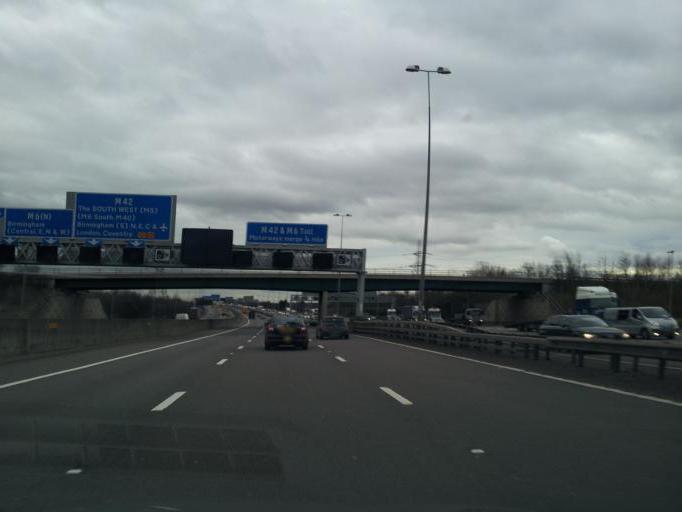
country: GB
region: England
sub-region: Warwickshire
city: Curdworth
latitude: 52.5296
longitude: -1.7295
